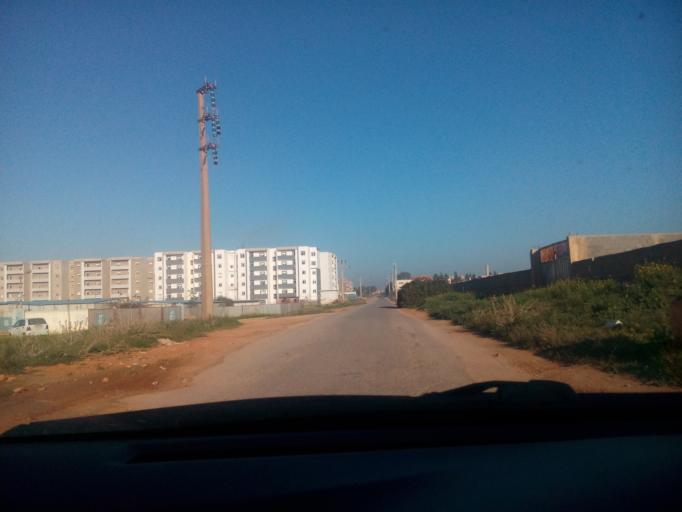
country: DZ
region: Oran
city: Bir el Djir
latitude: 35.7528
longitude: -0.5292
